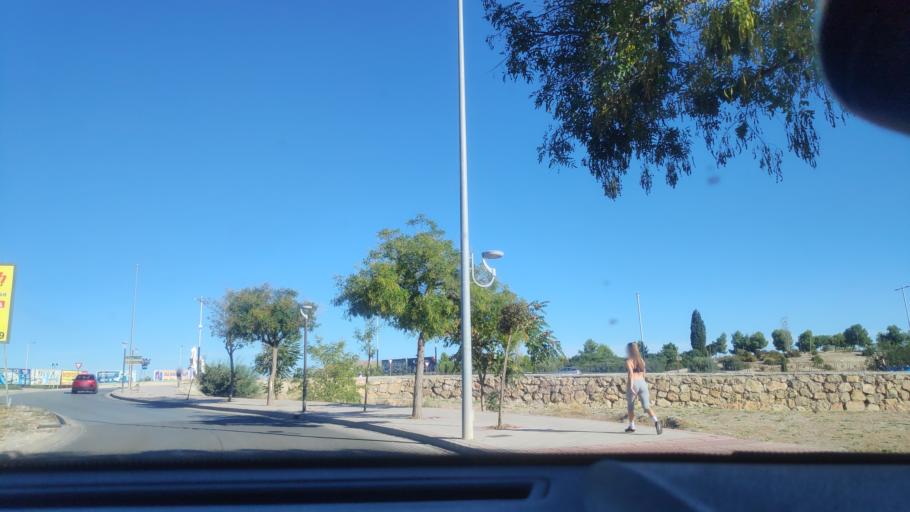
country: ES
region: Andalusia
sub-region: Provincia de Jaen
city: Jaen
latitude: 37.7906
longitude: -3.7905
